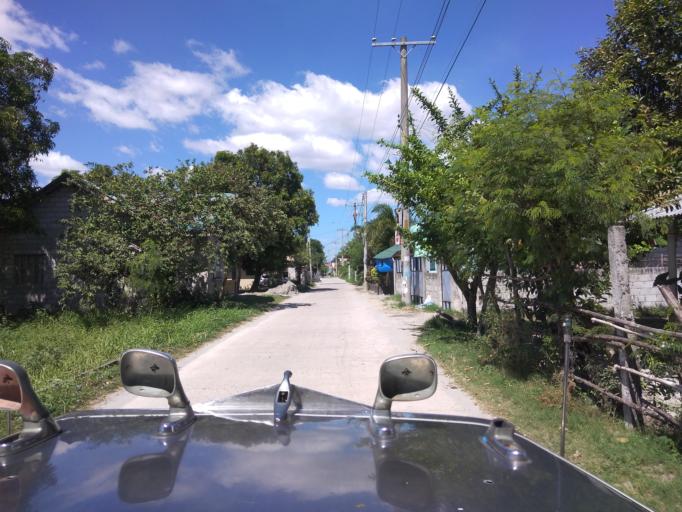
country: PH
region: Central Luzon
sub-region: Province of Pampanga
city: Magliman
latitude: 15.0492
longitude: 120.6422
